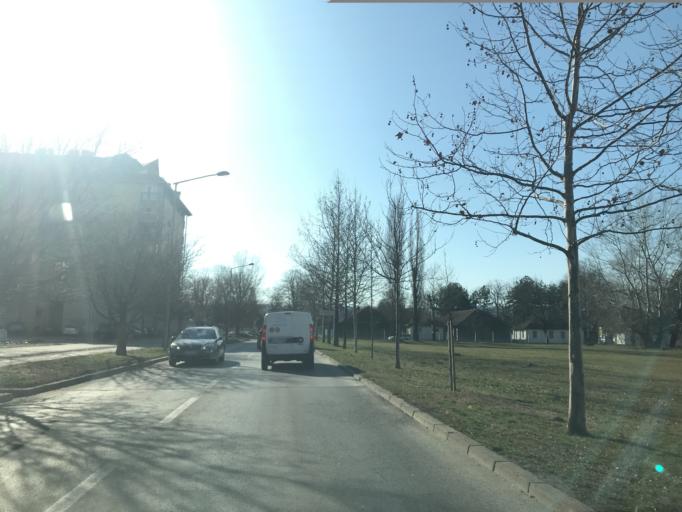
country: RS
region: Autonomna Pokrajina Vojvodina
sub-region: Juznobacki Okrug
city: Novi Sad
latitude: 45.2365
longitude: 19.8270
